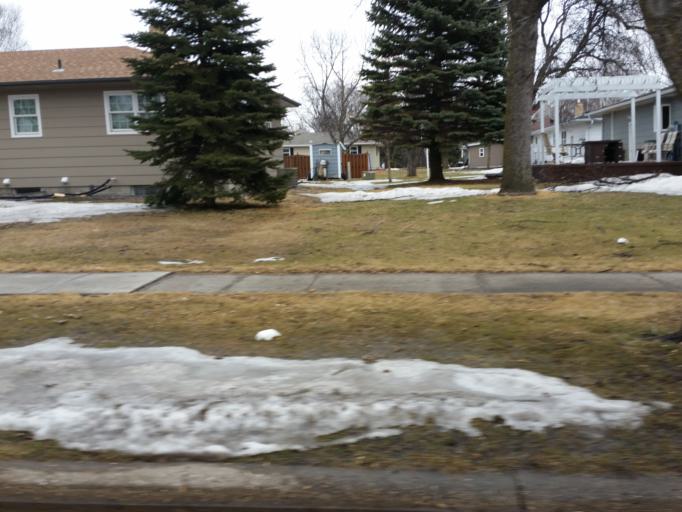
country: US
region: North Dakota
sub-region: Walsh County
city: Grafton
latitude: 48.4093
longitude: -97.4203
